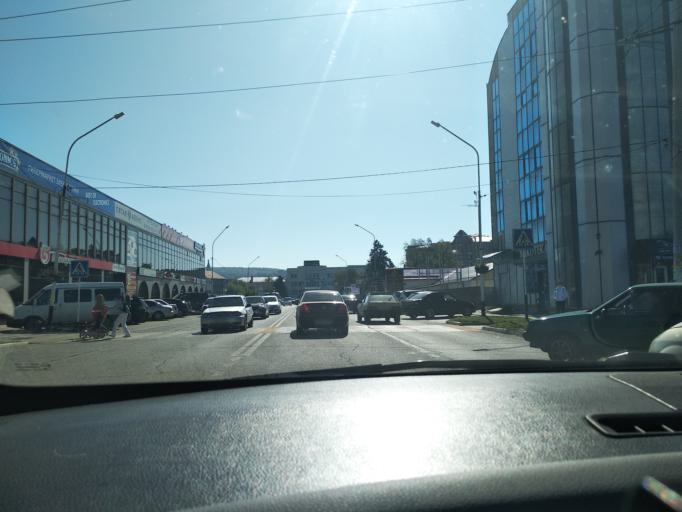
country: RU
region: Krasnodarskiy
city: Goryachiy Klyuch
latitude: 44.6355
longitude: 39.1350
